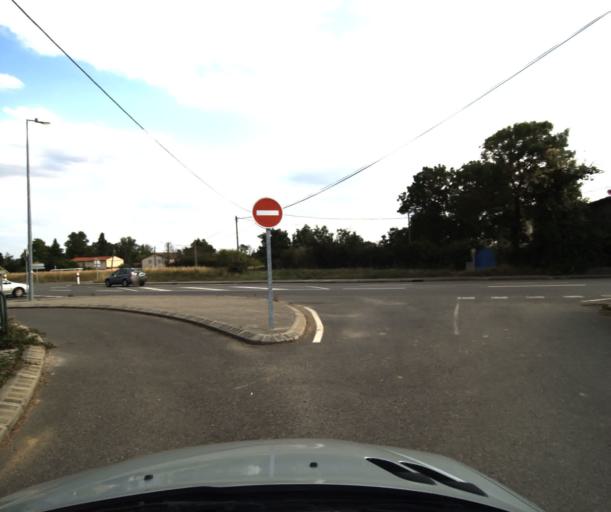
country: FR
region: Midi-Pyrenees
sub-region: Departement de la Haute-Garonne
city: Fonsorbes
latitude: 43.5133
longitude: 1.2125
